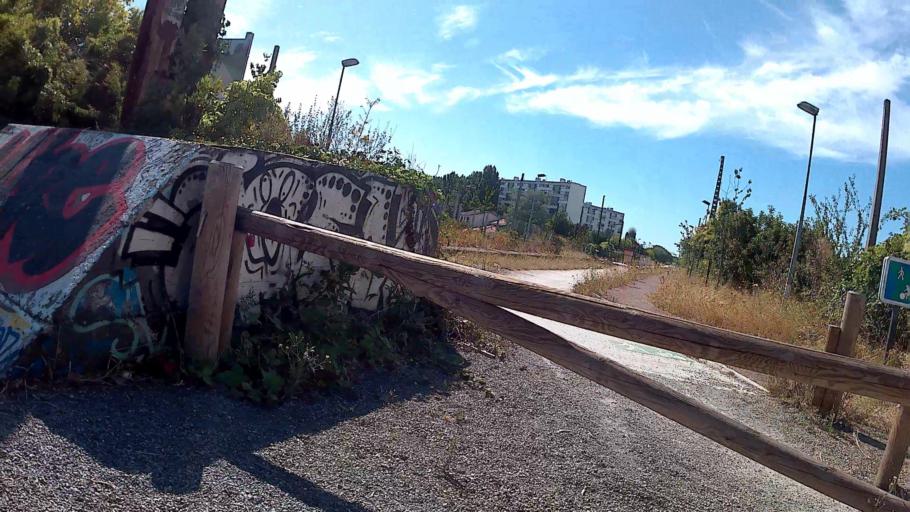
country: FR
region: Aquitaine
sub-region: Departement de la Gironde
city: Le Bouscat
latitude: 44.8666
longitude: -0.5771
